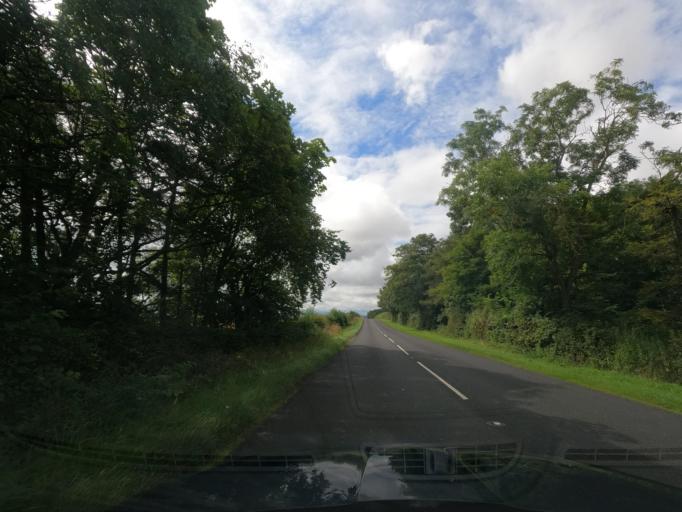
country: GB
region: England
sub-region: Northumberland
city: Ancroft
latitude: 55.7216
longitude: -1.9849
